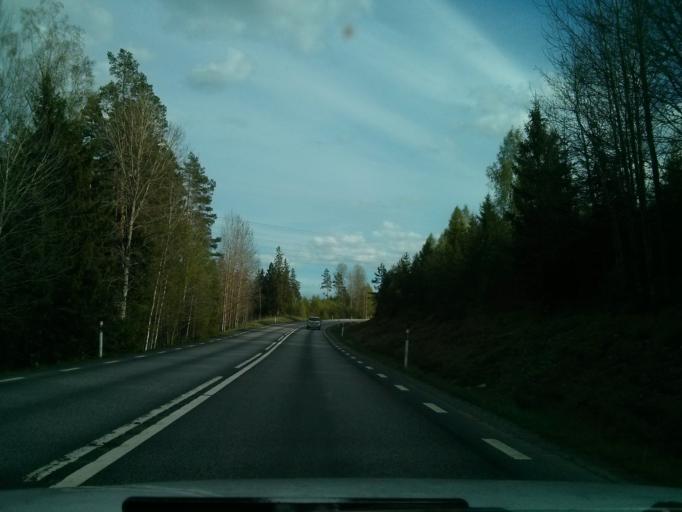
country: SE
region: Soedermanland
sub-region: Katrineholms Kommun
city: Katrineholm
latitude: 58.9306
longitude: 16.4091
